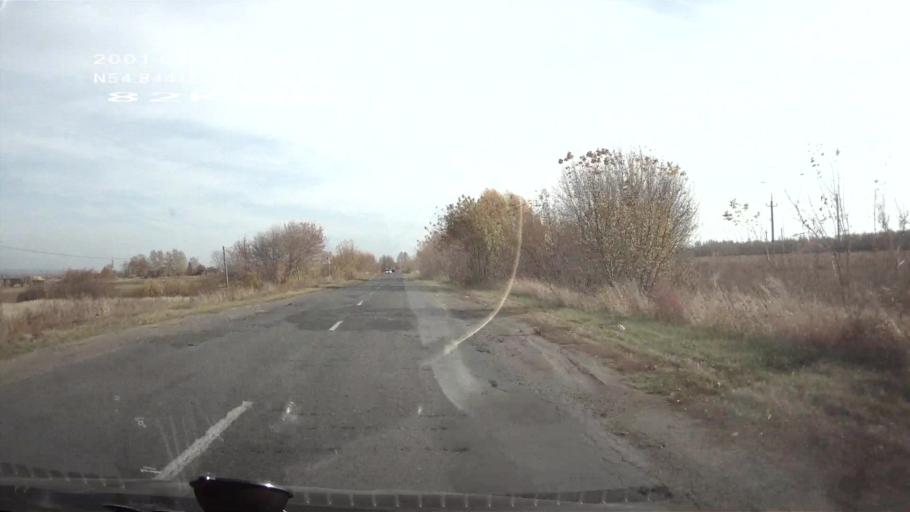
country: RU
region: Chuvashia
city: Alatyr'
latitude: 54.8441
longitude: 46.4681
